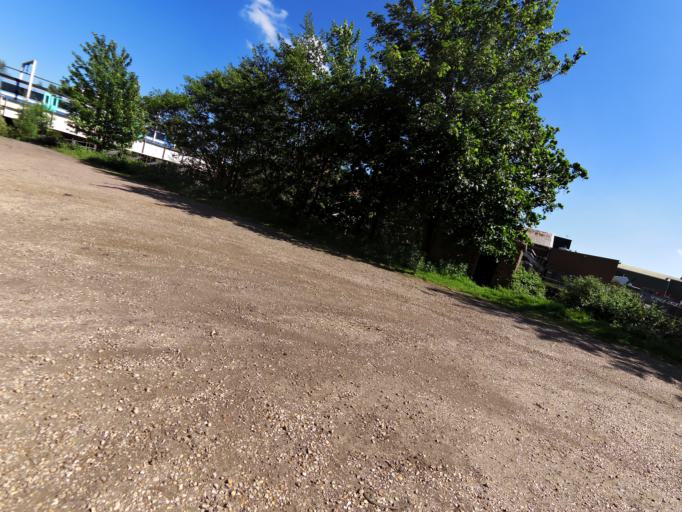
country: GB
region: England
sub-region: Norfolk
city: Thorpe Hamlet
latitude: 52.6202
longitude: 1.3149
